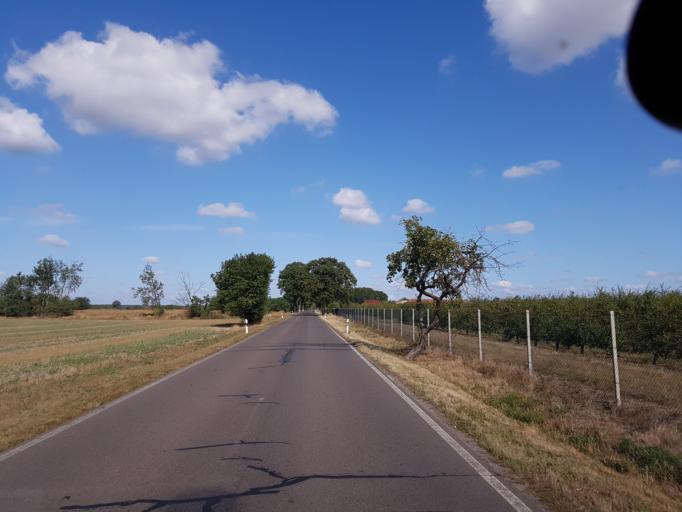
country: DE
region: Brandenburg
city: Sonnewalde
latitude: 51.7204
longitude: 13.6288
